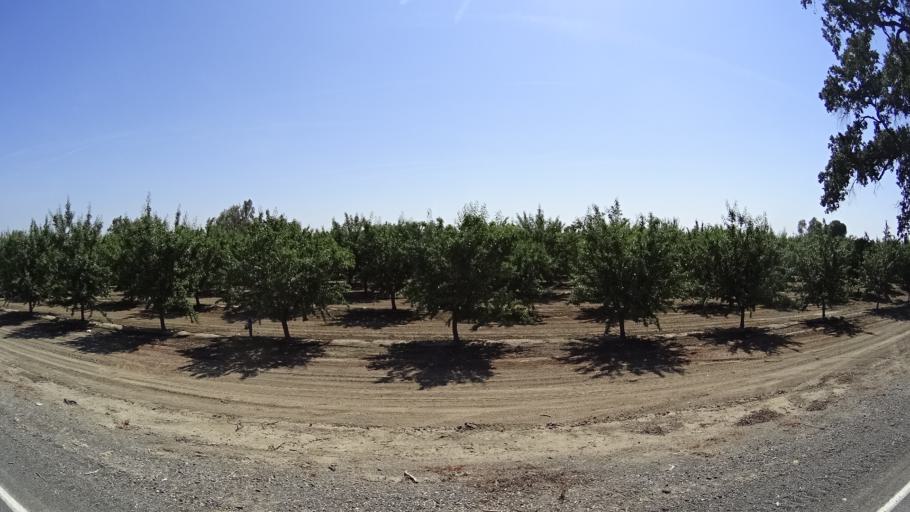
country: US
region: California
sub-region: Kings County
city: Lemoore
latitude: 36.3454
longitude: -119.8513
